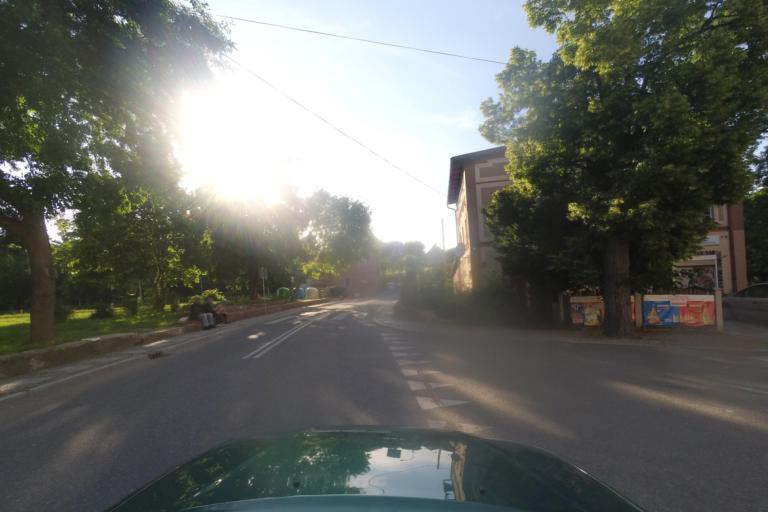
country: PL
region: Lower Silesian Voivodeship
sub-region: Powiat dzierzoniowski
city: Niemcza
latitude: 50.7198
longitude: 16.8356
